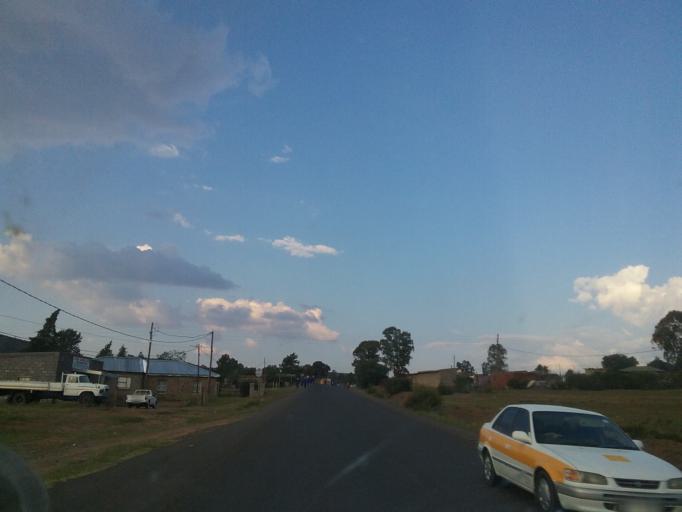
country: LS
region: Quthing
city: Quthing
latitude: -30.3975
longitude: 27.6626
